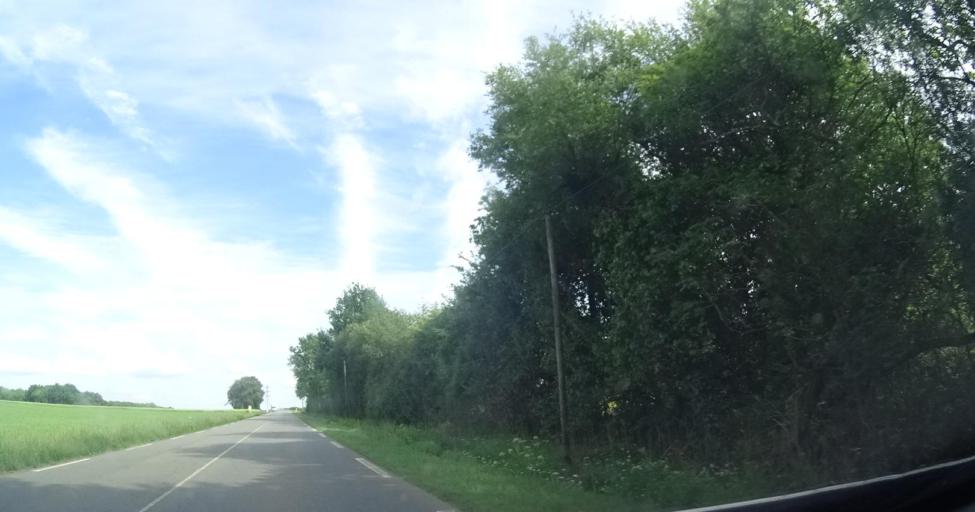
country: FR
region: Pays de la Loire
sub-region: Departement de la Loire-Atlantique
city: Fegreac
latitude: 47.6049
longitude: -2.0296
